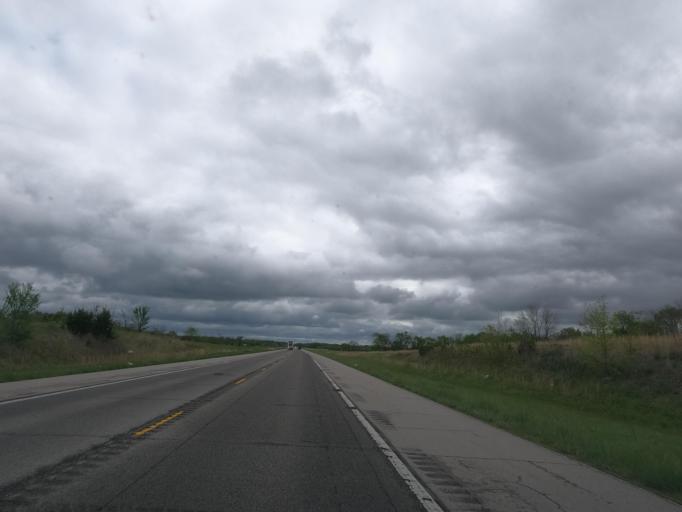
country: US
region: Kansas
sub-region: Labette County
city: Parsons
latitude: 37.3432
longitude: -95.3712
